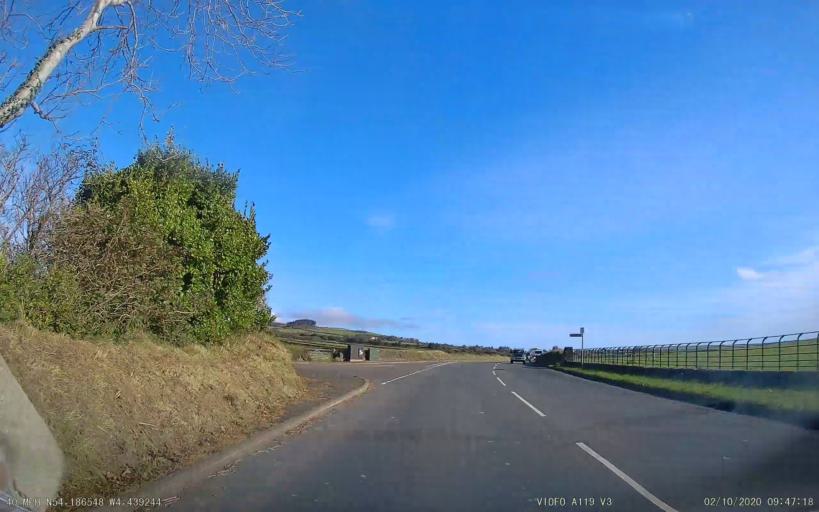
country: IM
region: Douglas
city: Douglas
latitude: 54.1865
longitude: -4.4393
